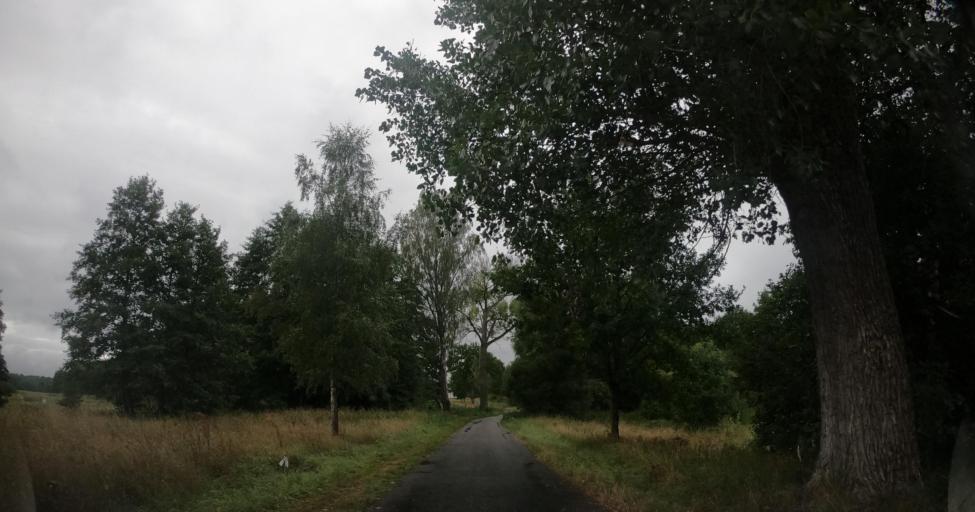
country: PL
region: West Pomeranian Voivodeship
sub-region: Powiat lobeski
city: Wegorzyno
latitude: 53.5344
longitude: 15.5039
